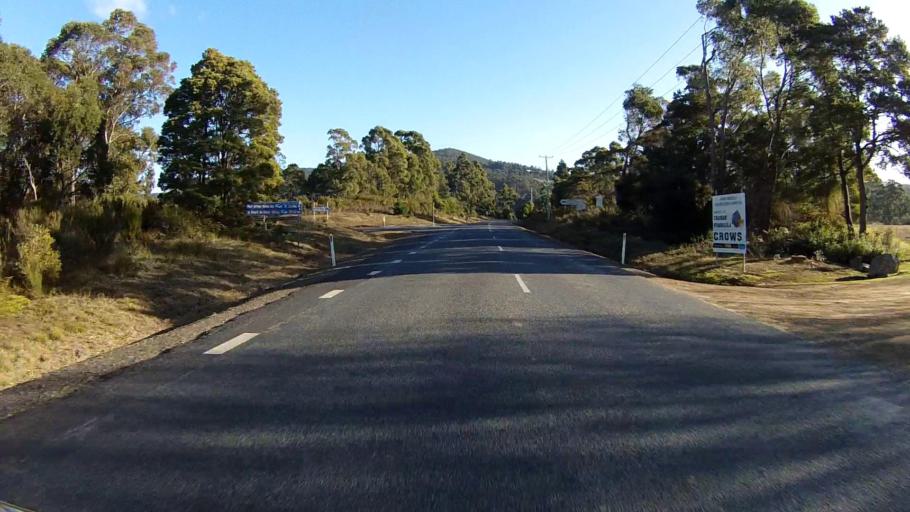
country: AU
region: Tasmania
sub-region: Clarence
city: Sandford
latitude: -43.1428
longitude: 147.8457
